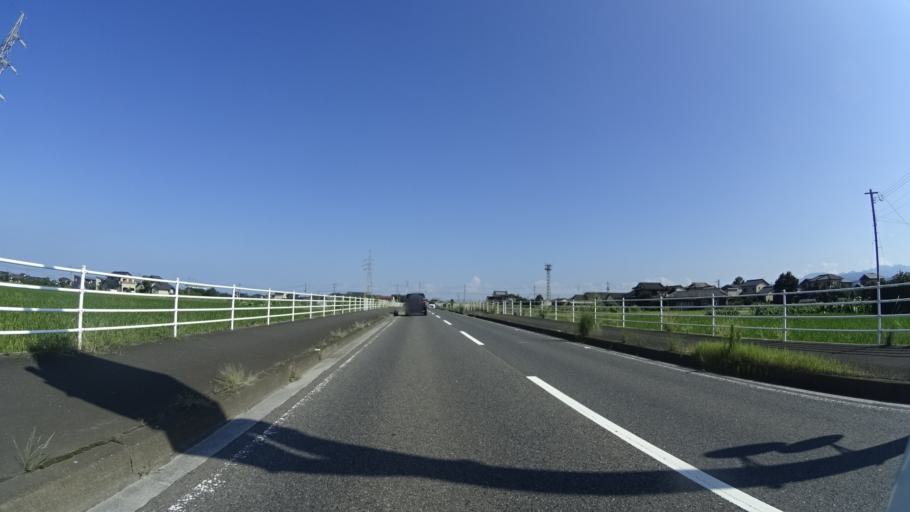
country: JP
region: Fukuoka
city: Tsuiki
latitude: 33.6681
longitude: 131.0235
